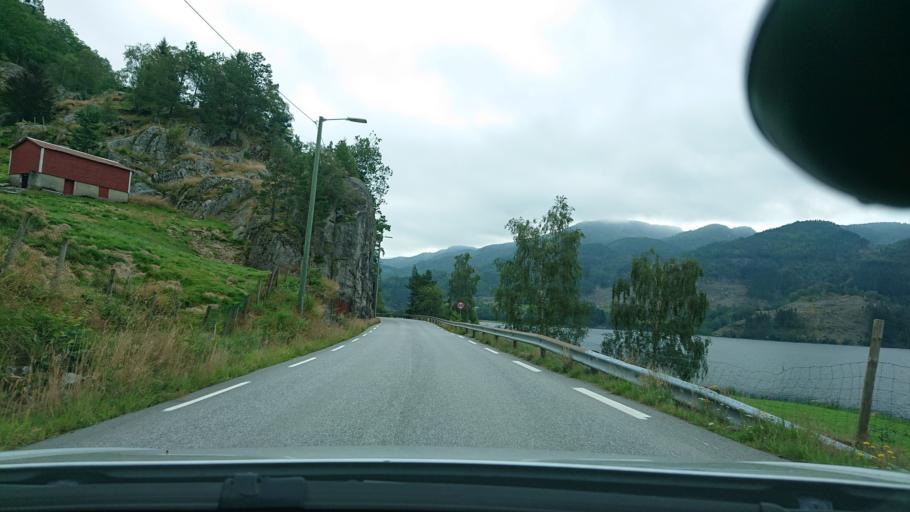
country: NO
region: Rogaland
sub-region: Hjelmeland
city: Hjelmelandsvagen
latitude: 59.2322
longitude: 6.1901
